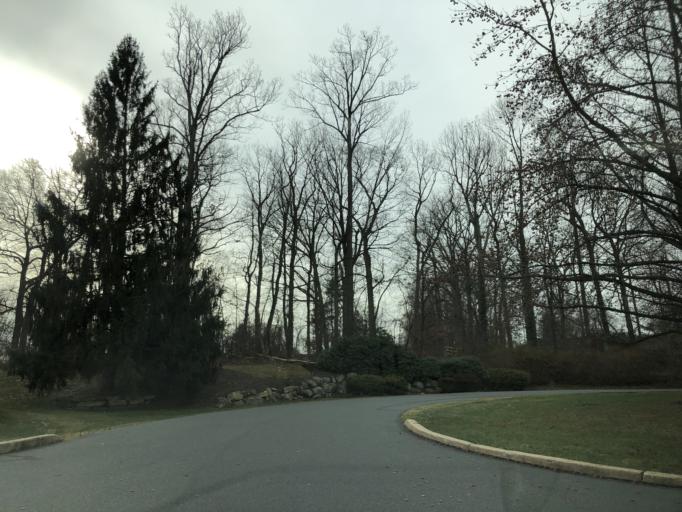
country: US
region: Pennsylvania
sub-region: Chester County
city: Exton
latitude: 40.0341
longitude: -75.6410
